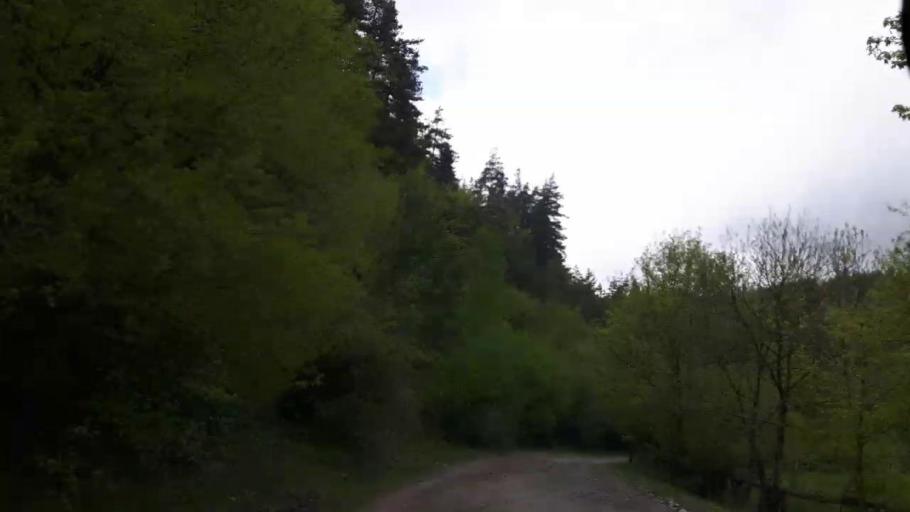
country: GE
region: Shida Kartli
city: Gori
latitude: 41.8613
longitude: 43.9551
